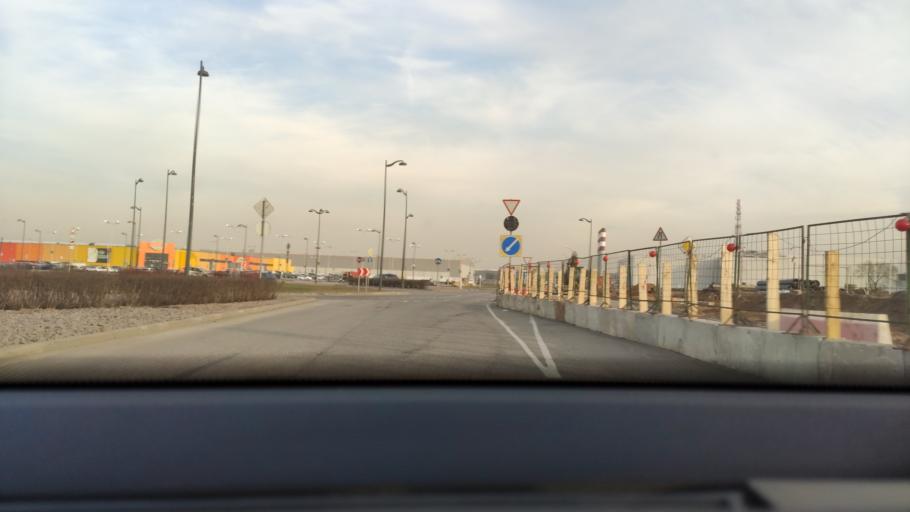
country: RU
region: Moskovskaya
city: Lyubertsy
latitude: 55.6587
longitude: 37.8795
